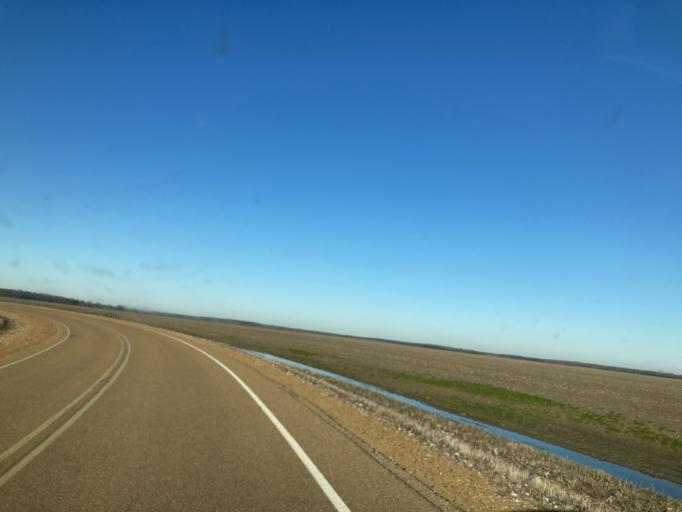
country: US
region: Mississippi
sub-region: Yazoo County
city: Yazoo City
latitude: 32.9311
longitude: -90.6010
